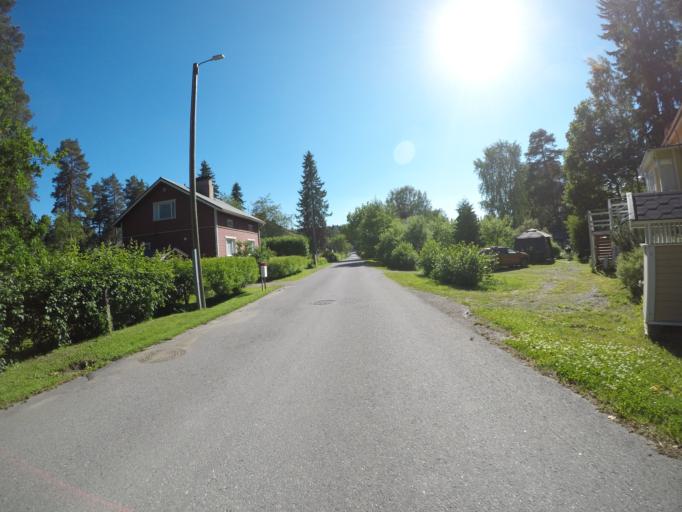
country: FI
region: Haeme
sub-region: Haemeenlinna
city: Haemeenlinna
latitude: 61.0123
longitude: 24.4756
